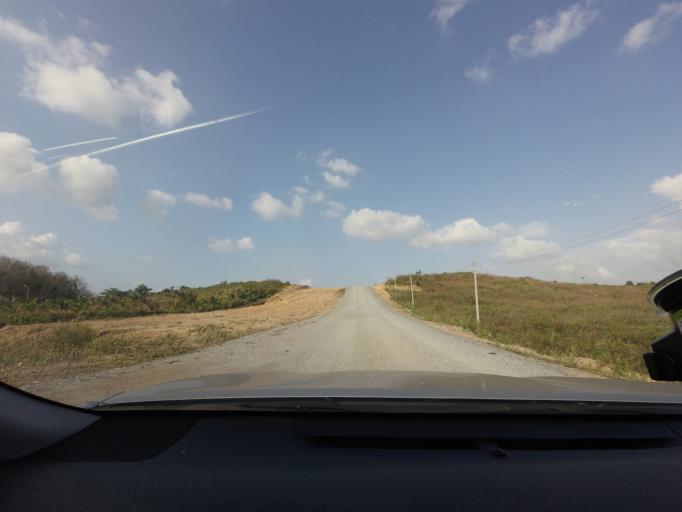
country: TH
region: Pattani
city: Mae Lan
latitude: 6.6110
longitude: 101.2551
